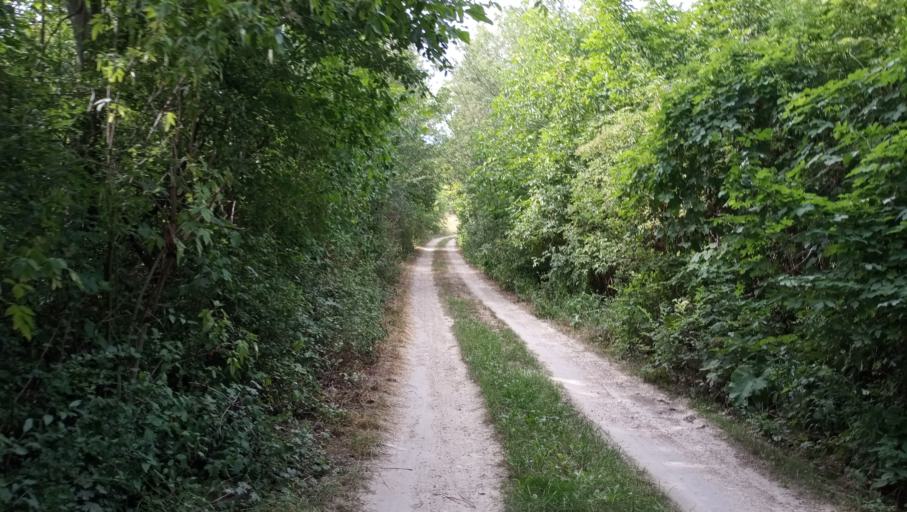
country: HU
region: Veszprem
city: Balatonkenese
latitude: 47.0408
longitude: 18.0874
